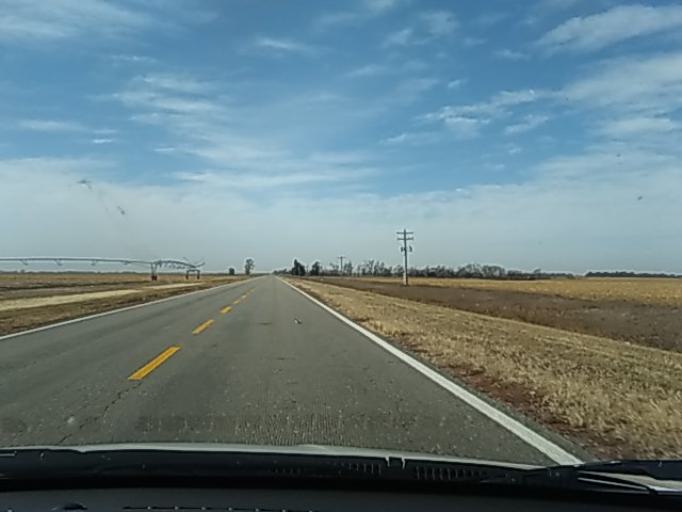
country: US
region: Nebraska
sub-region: Clay County
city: Clay Center
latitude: 40.4233
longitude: -98.0360
